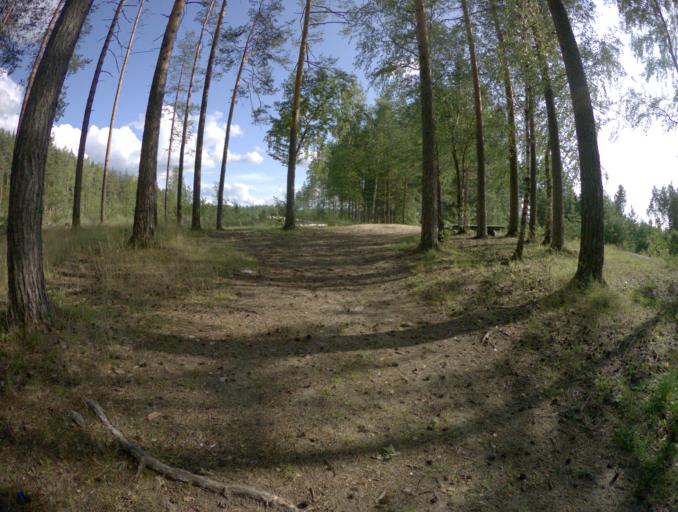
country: RU
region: Vladimir
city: Sobinka
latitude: 55.9601
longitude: 40.0592
